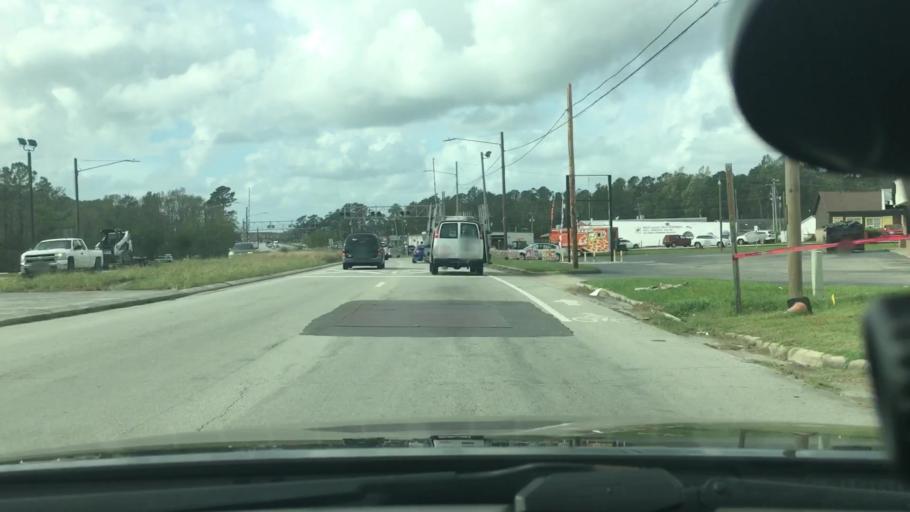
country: US
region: North Carolina
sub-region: Craven County
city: Havelock
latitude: 34.8801
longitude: -76.9059
